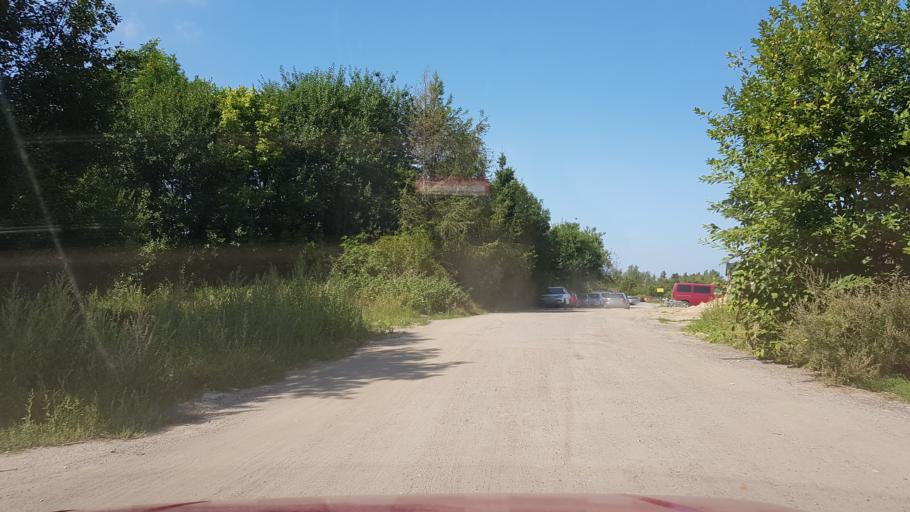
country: PL
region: West Pomeranian Voivodeship
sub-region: Koszalin
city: Koszalin
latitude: 54.2211
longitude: 16.1680
